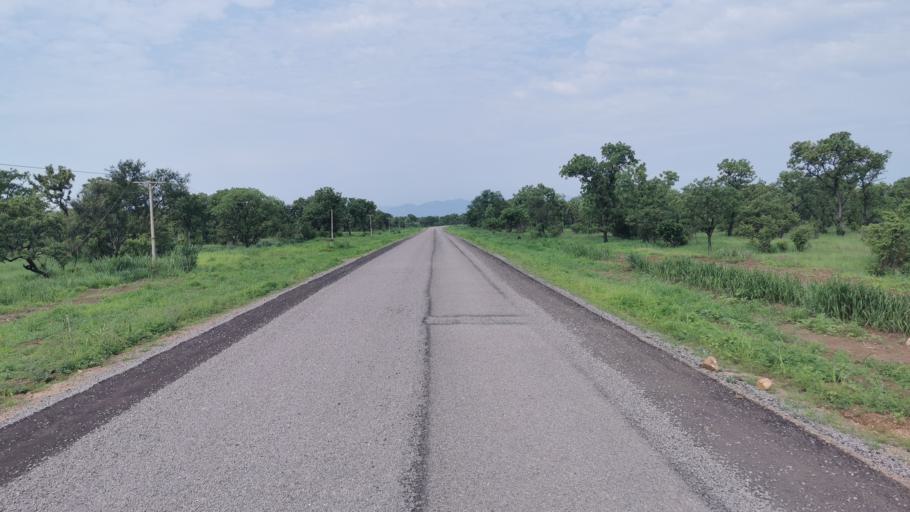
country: ET
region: Gambela
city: Gambela
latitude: 7.8367
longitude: 34.5582
